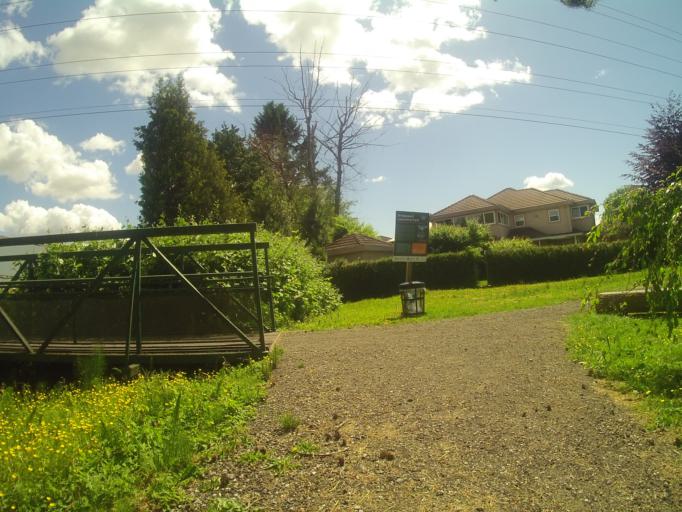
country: CA
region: British Columbia
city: Richmond
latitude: 49.1903
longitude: -123.0850
